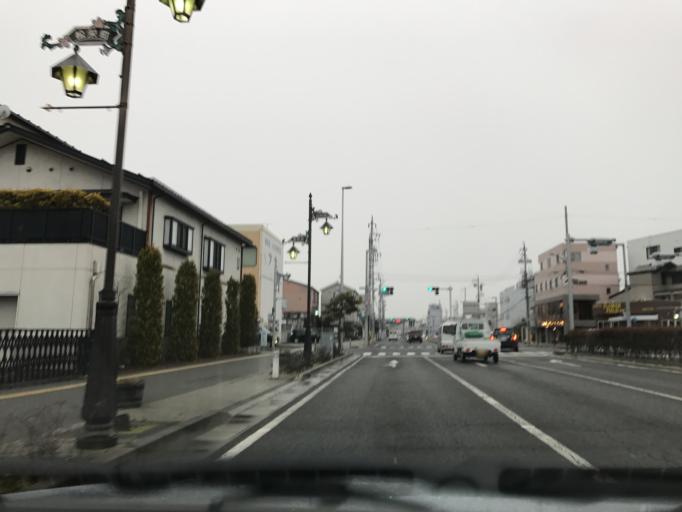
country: JP
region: Nagano
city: Matsumoto
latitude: 36.2372
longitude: 137.9657
